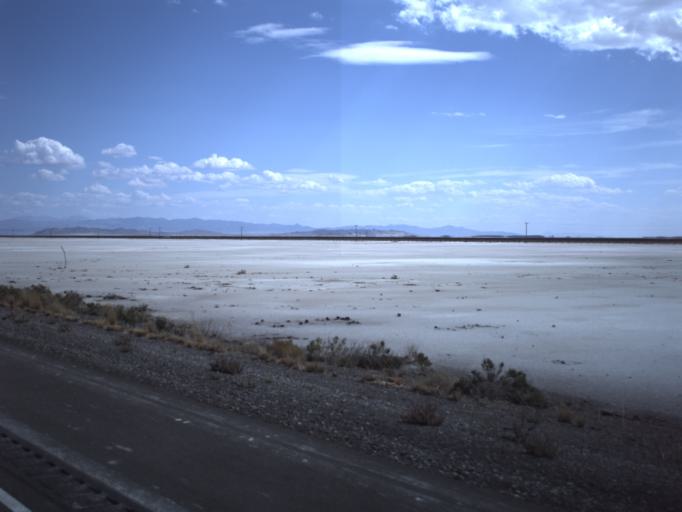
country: US
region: Utah
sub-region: Tooele County
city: Wendover
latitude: 40.7301
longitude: -113.4637
